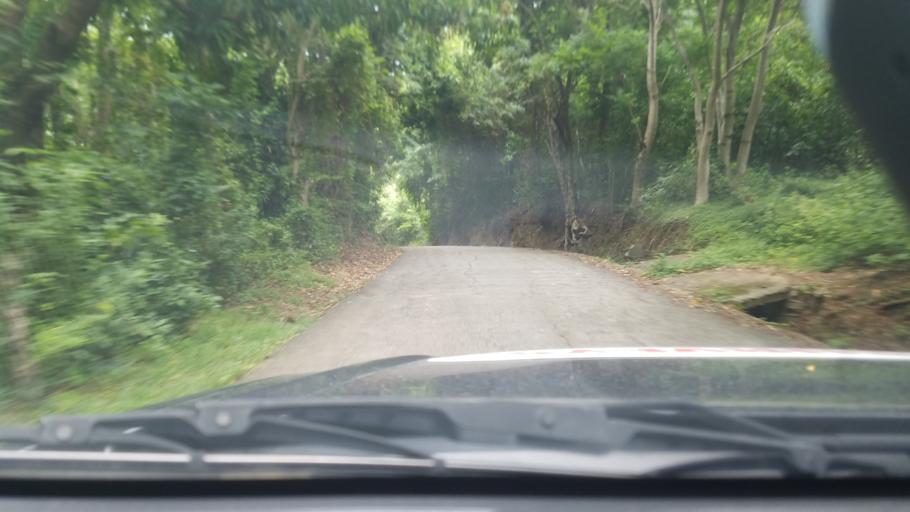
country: LC
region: Soufriere
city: Soufriere
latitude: 13.8377
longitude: -61.0612
